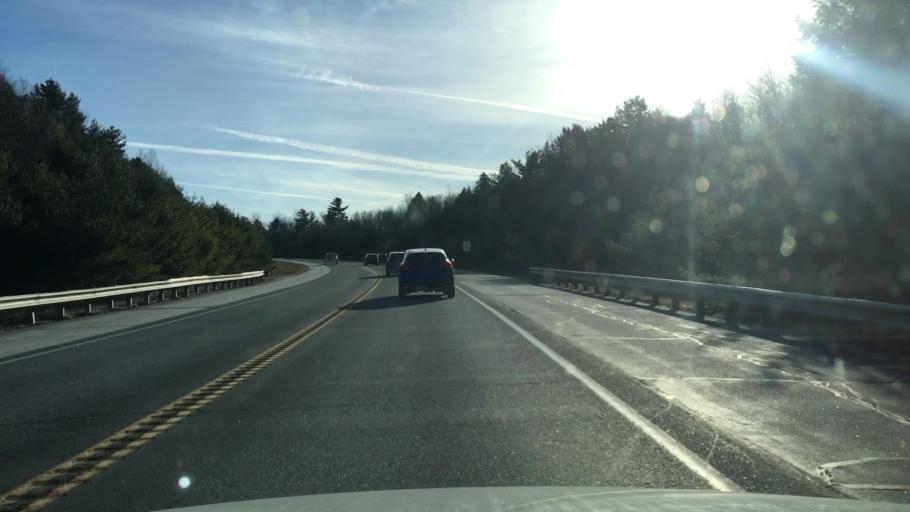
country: US
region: Maine
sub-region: Hancock County
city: Dedham
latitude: 44.6763
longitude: -68.5787
